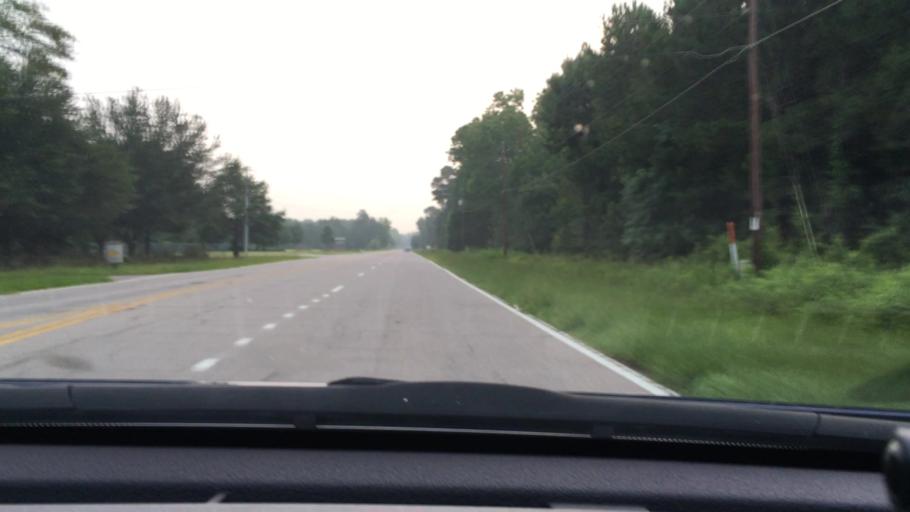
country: US
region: South Carolina
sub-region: Sumter County
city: East Sumter
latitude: 33.9497
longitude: -80.3108
